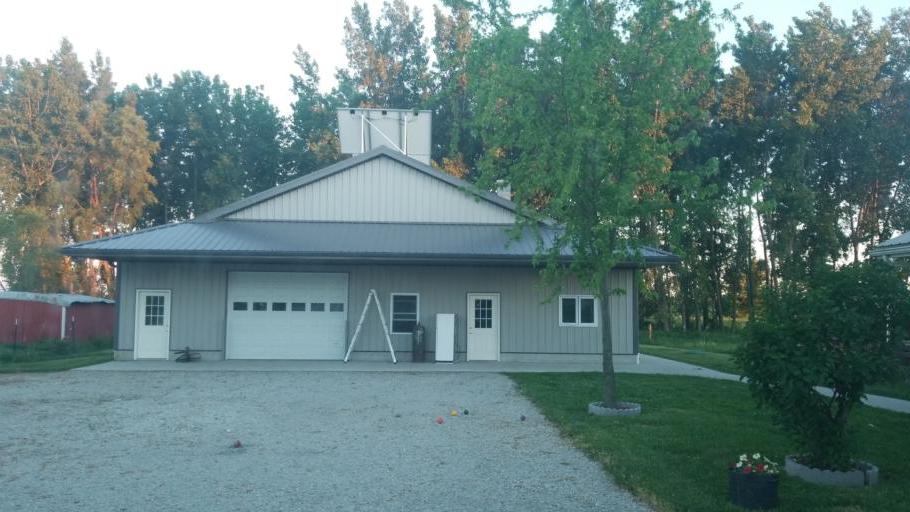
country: US
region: Indiana
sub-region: Elkhart County
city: Nappanee
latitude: 41.3611
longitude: -85.9819
